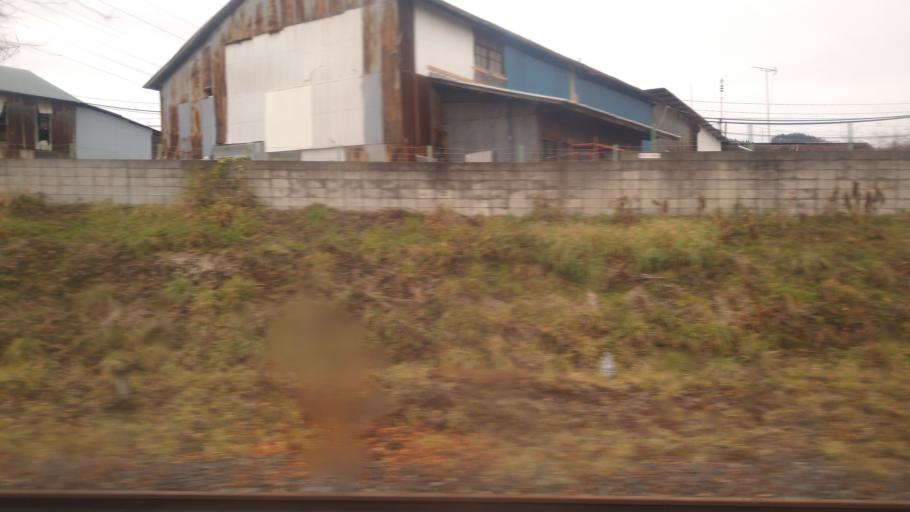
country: JP
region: Nagano
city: Shiojiri
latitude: 36.1105
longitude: 137.9447
